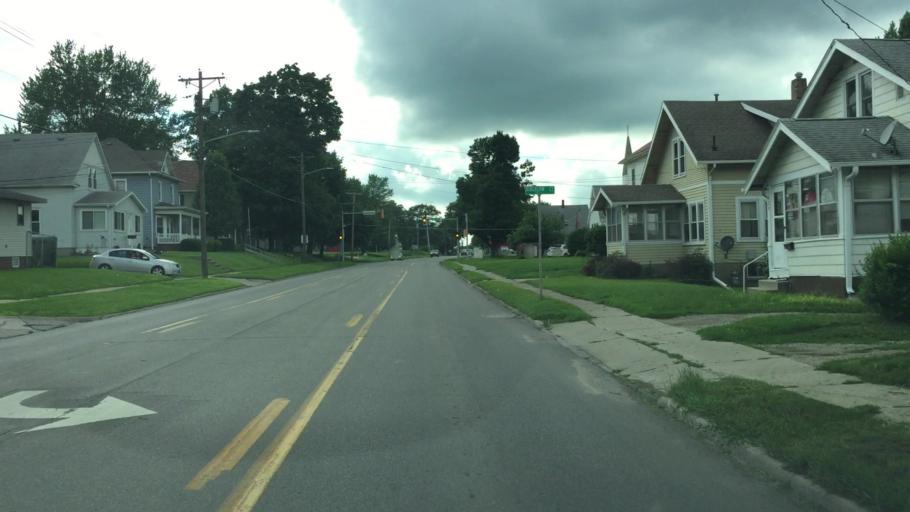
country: US
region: Iowa
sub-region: Jasper County
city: Newton
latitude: 41.6993
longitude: -93.0420
